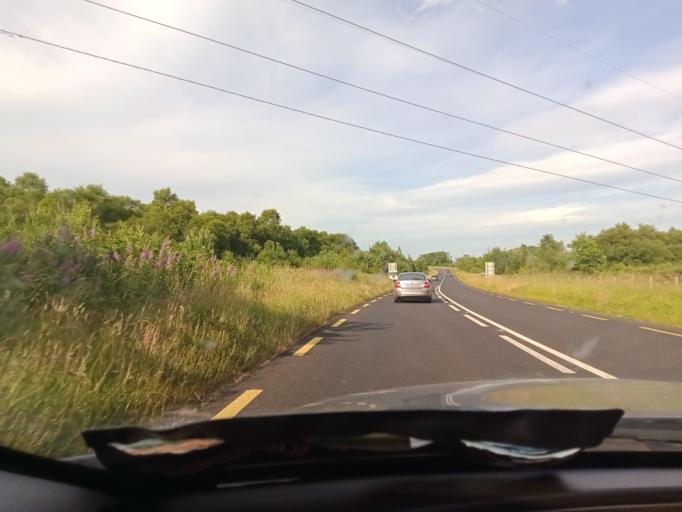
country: IE
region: Ulster
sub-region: An Cabhan
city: Cavan
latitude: 53.9136
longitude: -7.4343
